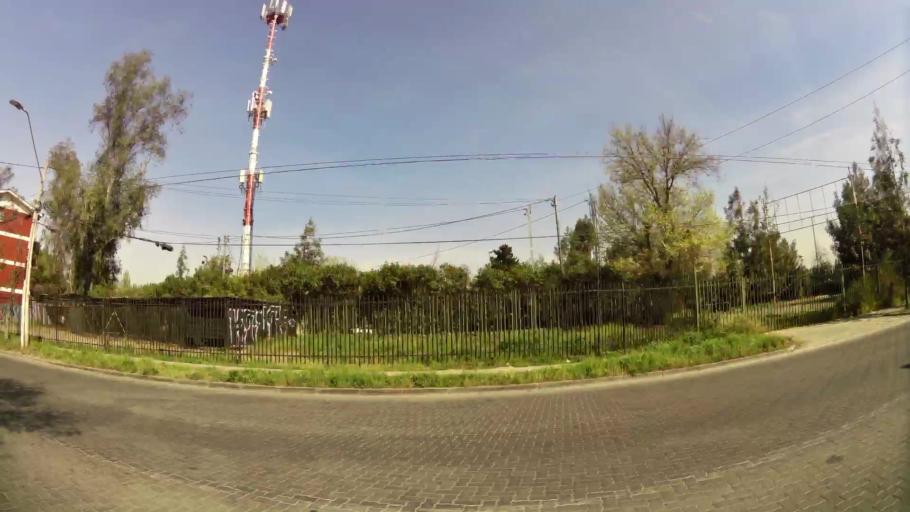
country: CL
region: Santiago Metropolitan
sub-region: Provincia de Santiago
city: Villa Presidente Frei, Nunoa, Santiago, Chile
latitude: -33.4975
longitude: -70.5921
